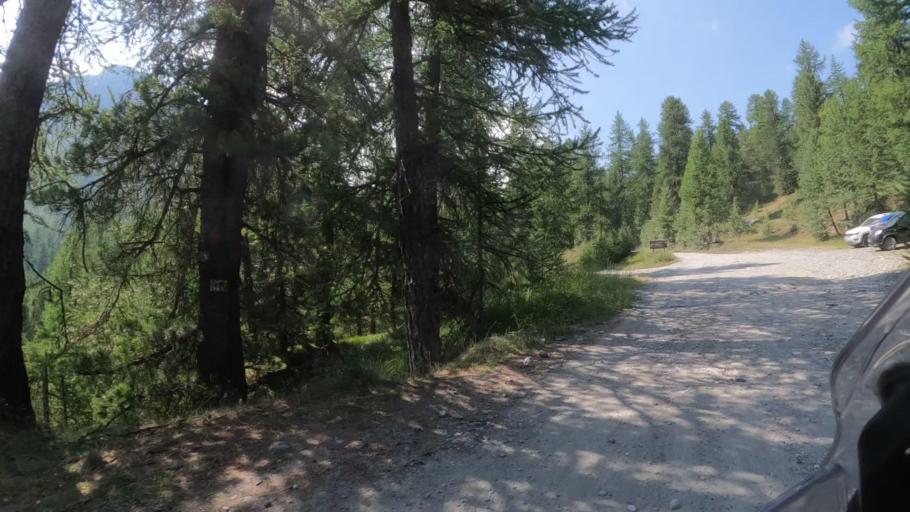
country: IT
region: Piedmont
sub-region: Provincia di Torino
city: Cesana Torinese
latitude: 44.9110
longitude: 6.8004
